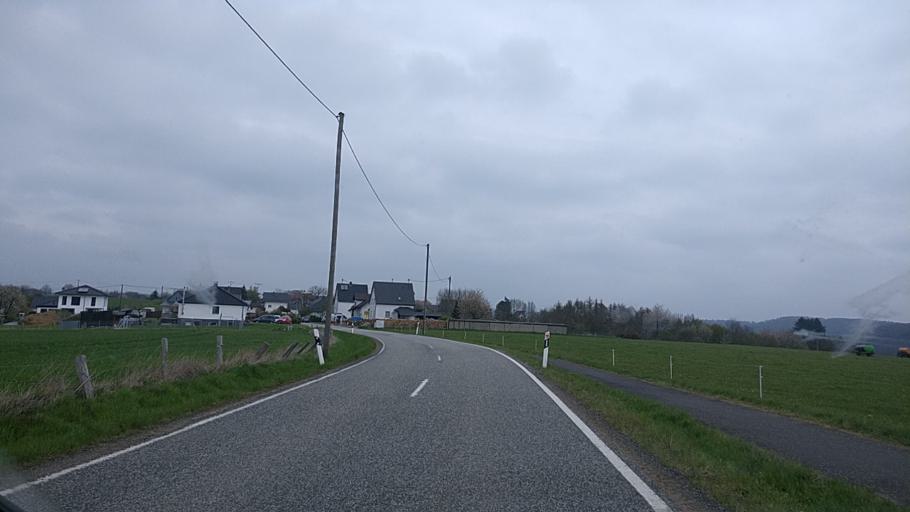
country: DE
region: Rheinland-Pfalz
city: Peterslahr
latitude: 50.6294
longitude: 7.4572
